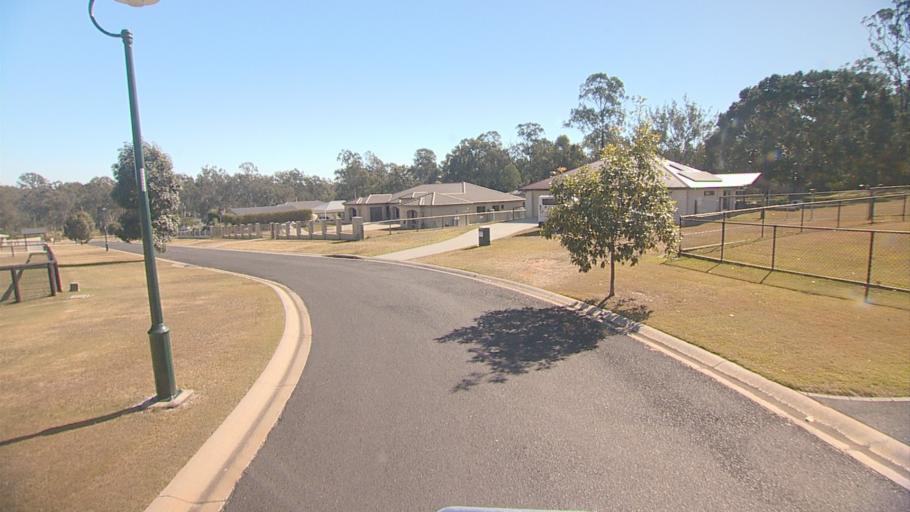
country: AU
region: Queensland
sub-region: Logan
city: Chambers Flat
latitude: -27.7876
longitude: 153.0993
